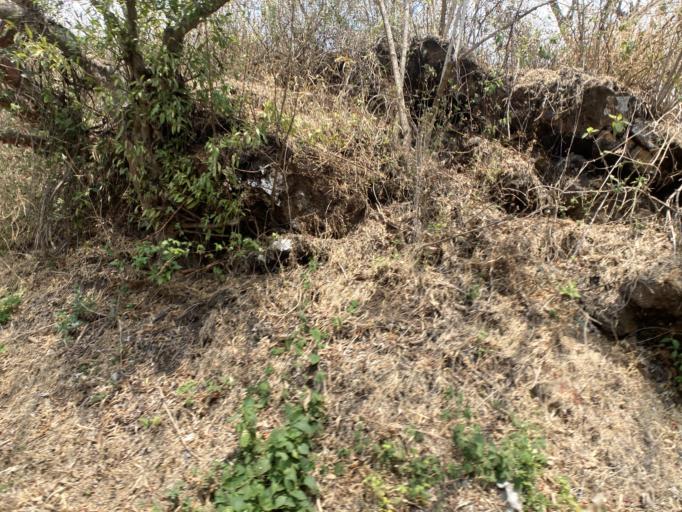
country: GT
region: Escuintla
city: San Vicente Pacaya
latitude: 14.3769
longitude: -90.5545
